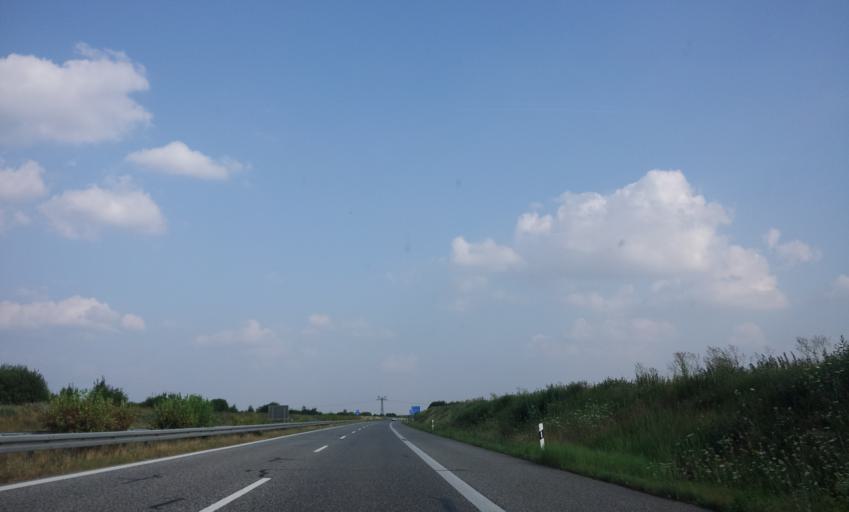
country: DE
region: Mecklenburg-Vorpommern
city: Jatznick
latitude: 53.5027
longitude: 13.8990
